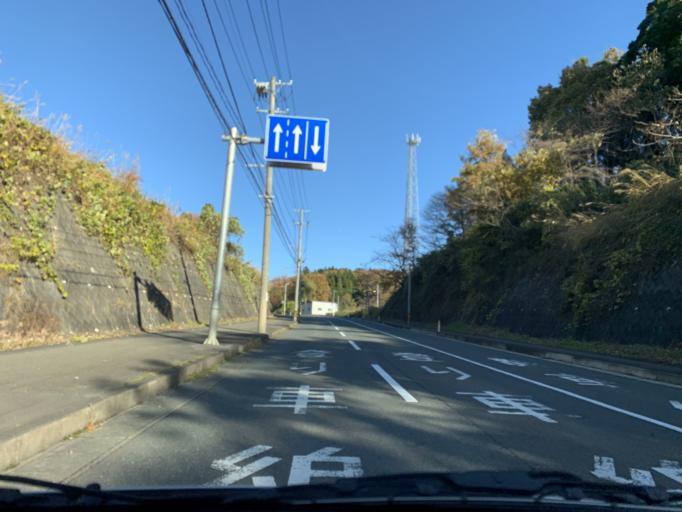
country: JP
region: Iwate
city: Mizusawa
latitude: 39.2014
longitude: 141.1738
